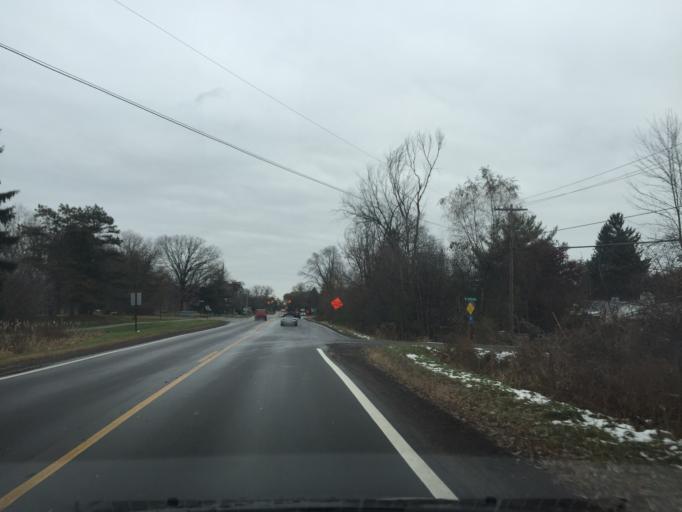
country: US
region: Michigan
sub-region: Oakland County
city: Franklin
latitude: 42.5301
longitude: -83.2887
